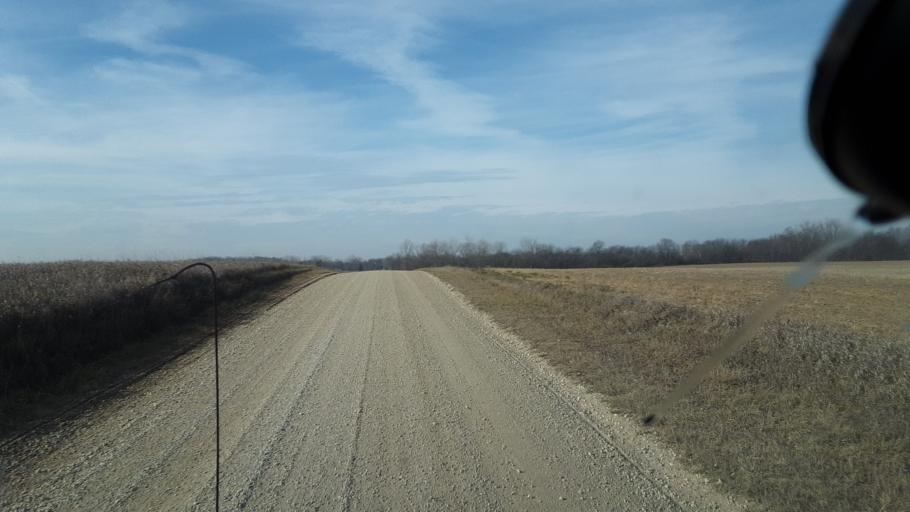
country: US
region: Ohio
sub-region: Defiance County
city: Hicksville
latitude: 41.2708
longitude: -84.8157
